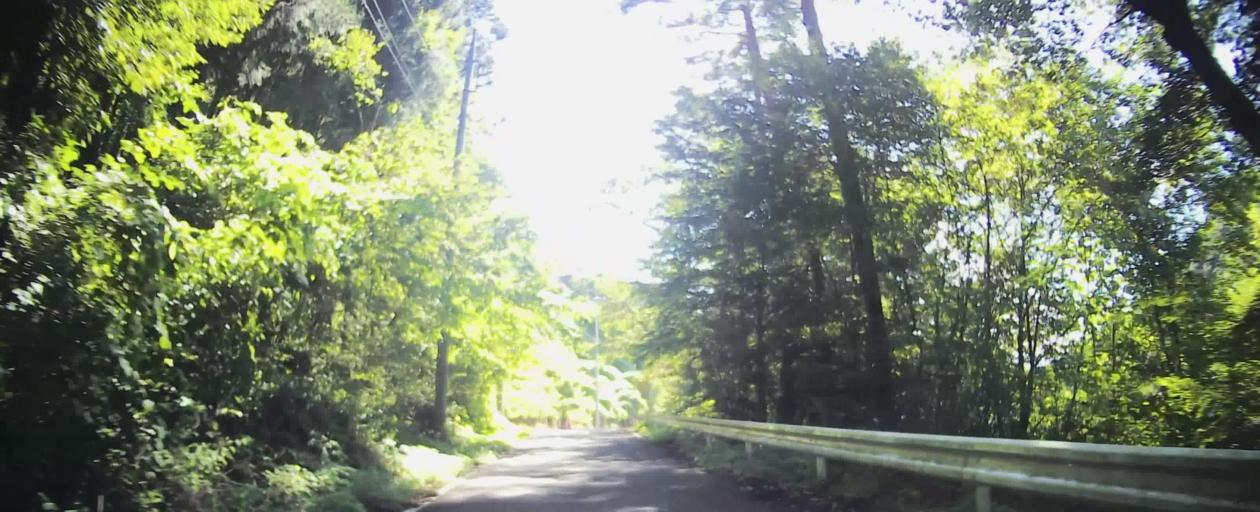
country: JP
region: Gunma
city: Nakanojomachi
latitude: 36.5670
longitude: 138.7309
